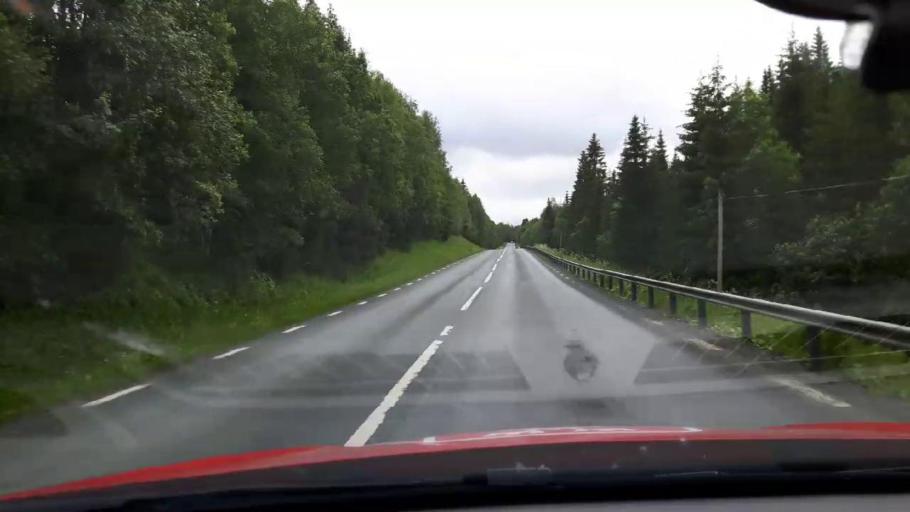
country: SE
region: Jaemtland
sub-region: Are Kommun
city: Are
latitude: 63.3932
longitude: 12.7778
